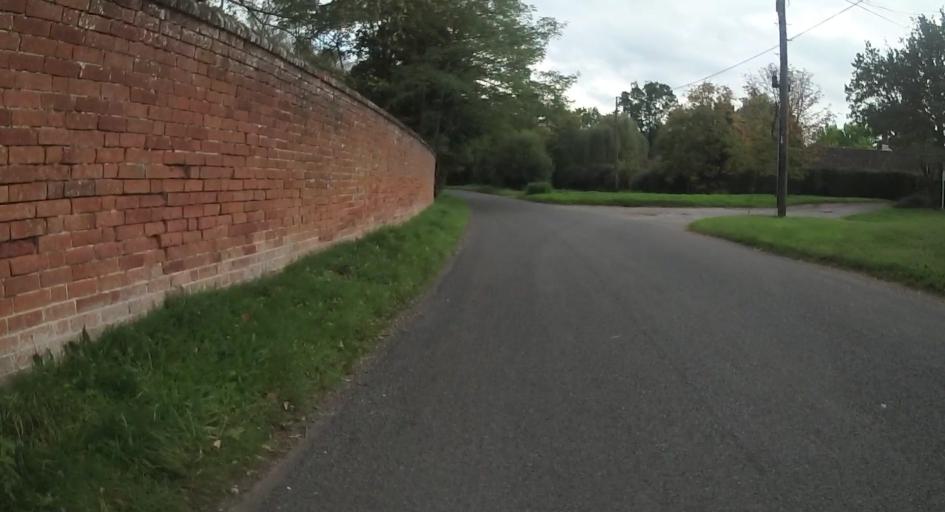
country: GB
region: England
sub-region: Hampshire
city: Hook
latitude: 51.3076
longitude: -0.9314
